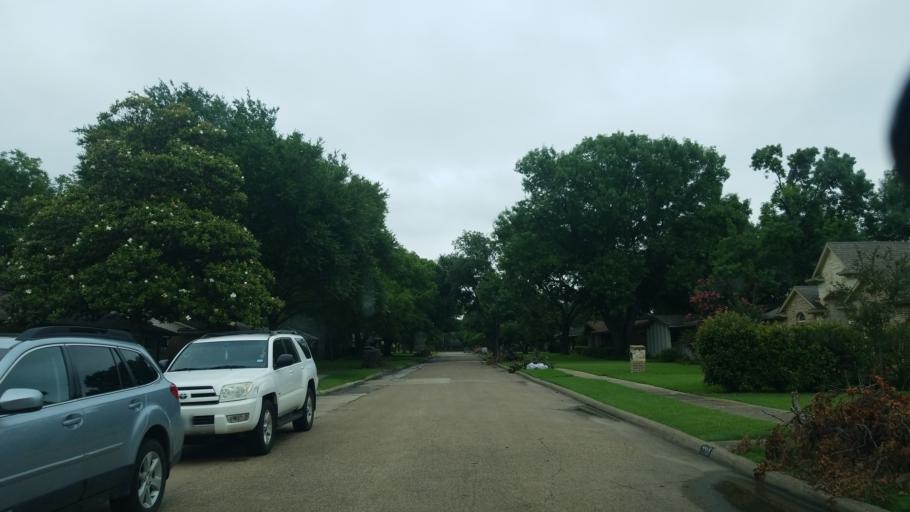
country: US
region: Texas
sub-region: Dallas County
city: Farmers Branch
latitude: 32.8979
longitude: -96.8674
